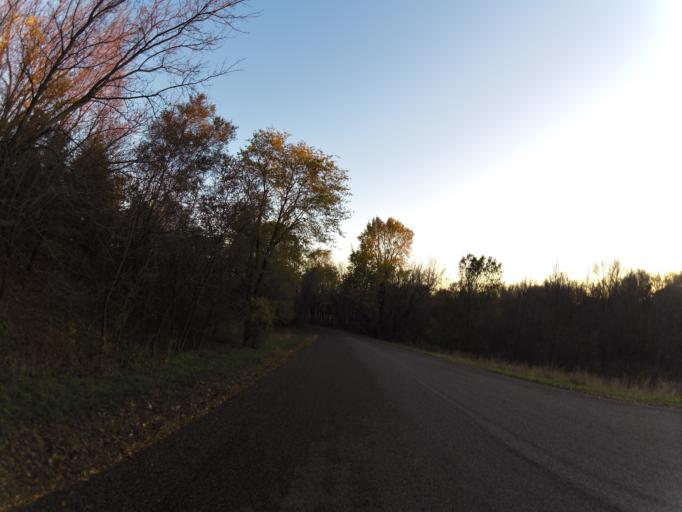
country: US
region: Minnesota
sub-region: Olmsted County
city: Rochester
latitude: 44.0458
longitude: -92.4079
